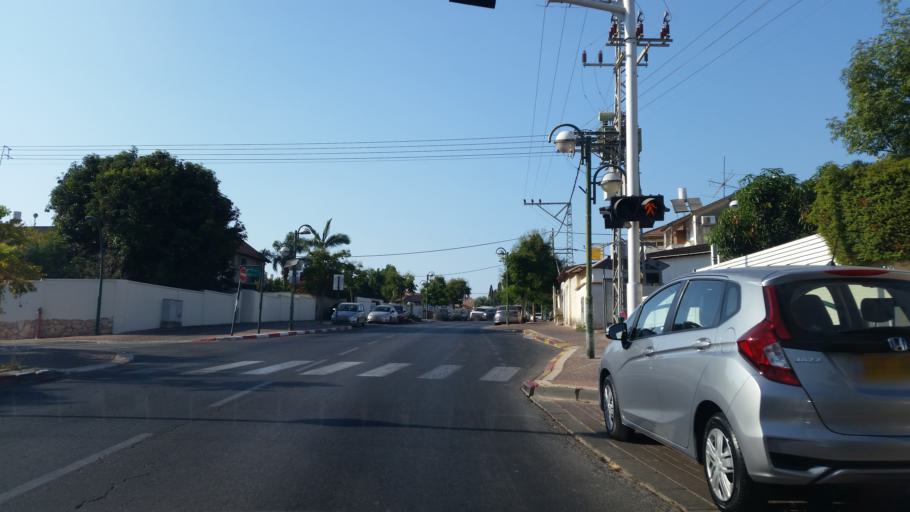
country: IL
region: Tel Aviv
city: Ramat HaSharon
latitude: 32.1326
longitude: 34.8527
